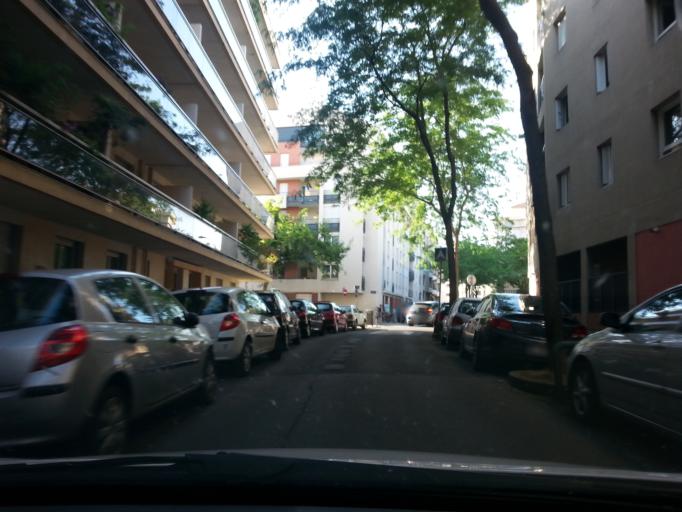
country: FR
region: Rhone-Alpes
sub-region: Departement du Rhone
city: Lyon
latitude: 45.7466
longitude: 4.8567
